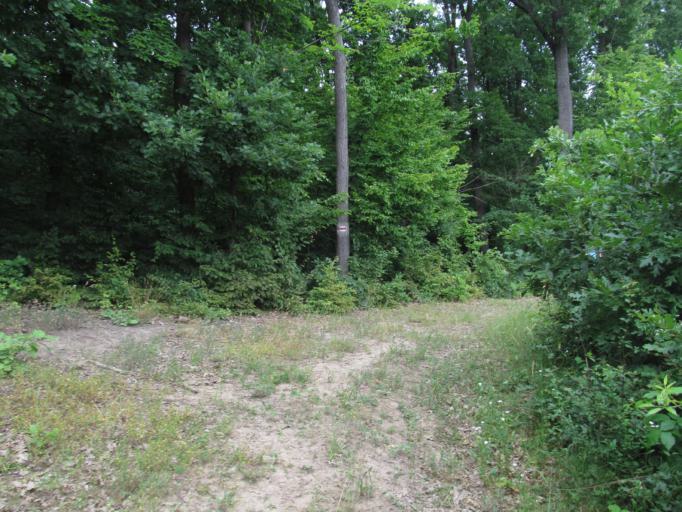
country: HU
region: Borsod-Abauj-Zemplen
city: Jardanhaza
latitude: 48.1621
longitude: 20.1577
